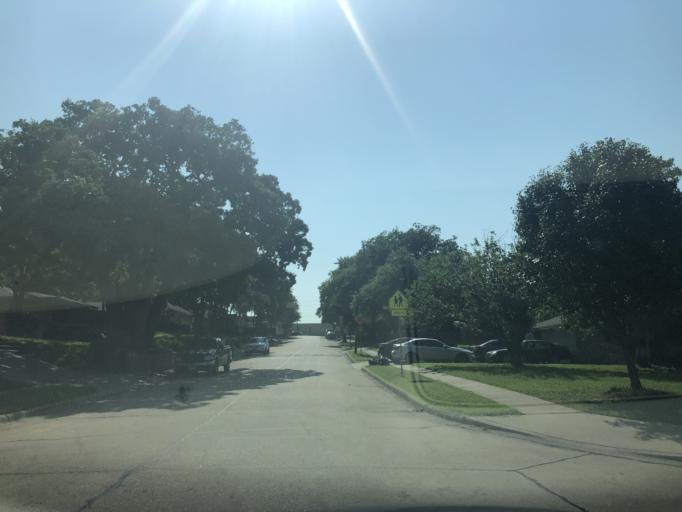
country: US
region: Texas
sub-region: Dallas County
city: Irving
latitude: 32.7966
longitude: -96.9609
